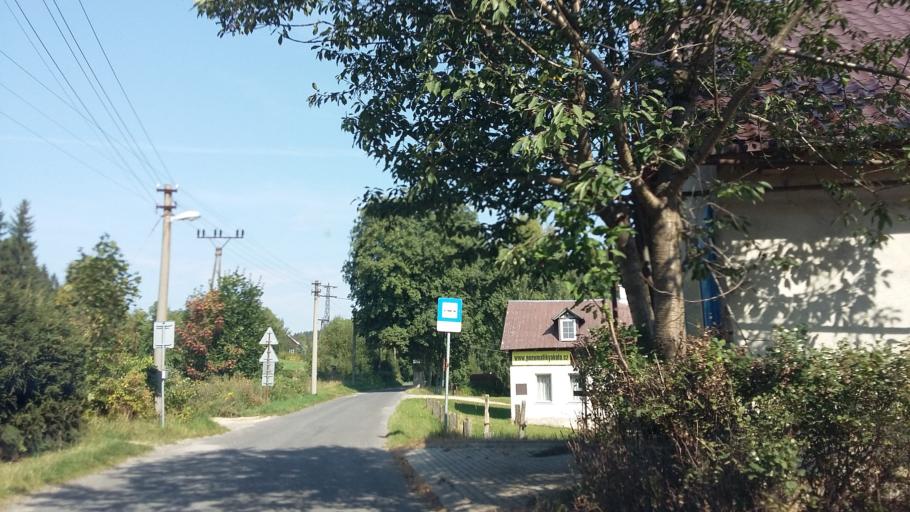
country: CZ
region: Liberecky
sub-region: Okres Jablonec nad Nisou
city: Lucany nad Nisou
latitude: 50.7488
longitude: 15.1956
